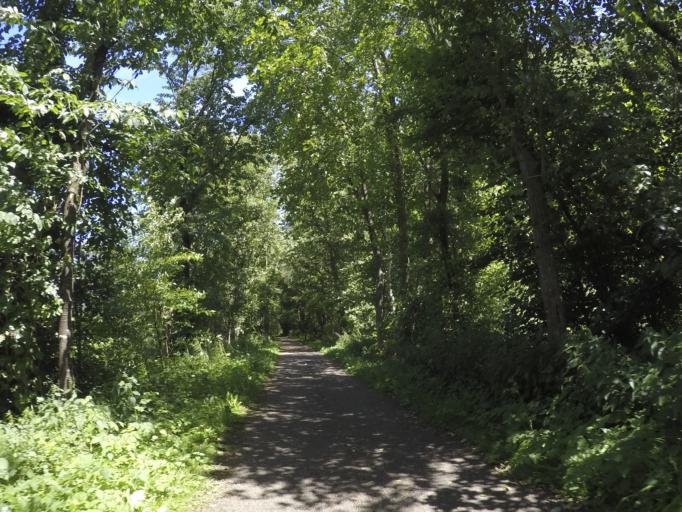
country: BE
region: Wallonia
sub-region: Province de Namur
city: Hamois
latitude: 50.3246
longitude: 5.1247
